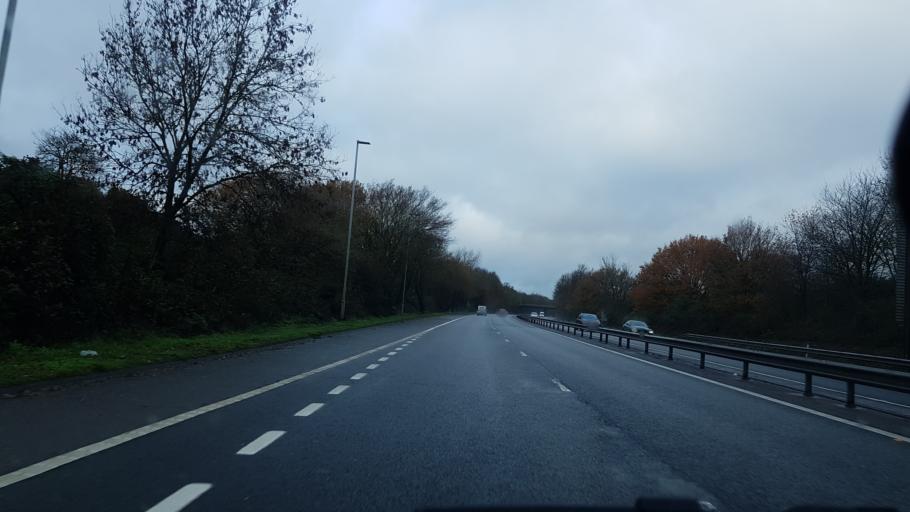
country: GB
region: England
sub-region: Bracknell Forest
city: Binfield
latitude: 51.4154
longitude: -0.8035
